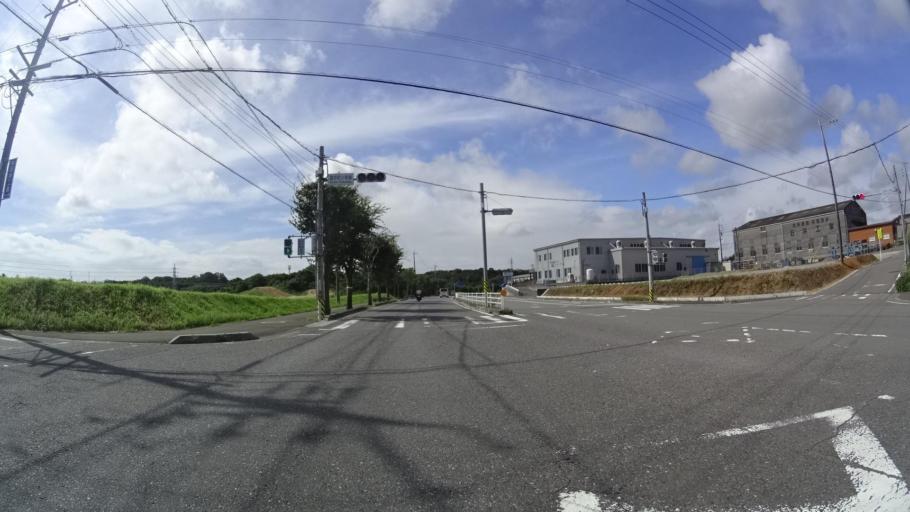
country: JP
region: Mie
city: Kawage
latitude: 34.8538
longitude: 136.5218
